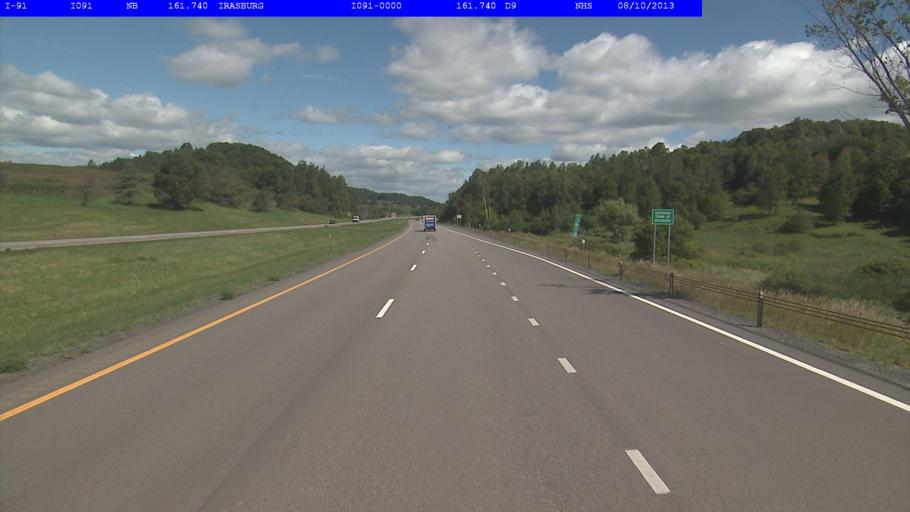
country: US
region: Vermont
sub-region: Orleans County
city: Newport
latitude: 44.8110
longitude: -72.2108
